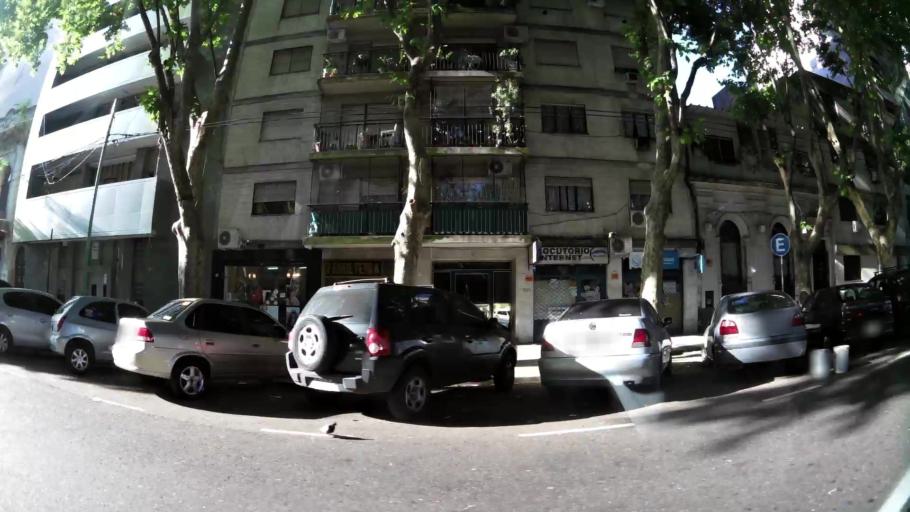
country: AR
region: Buenos Aires F.D.
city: Colegiales
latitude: -34.6148
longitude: -58.4266
